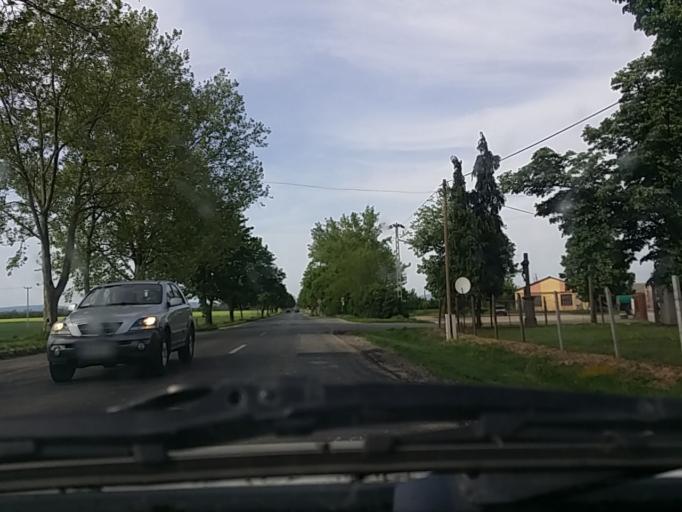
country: HU
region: Baranya
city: Harkany
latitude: 45.9219
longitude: 18.2337
